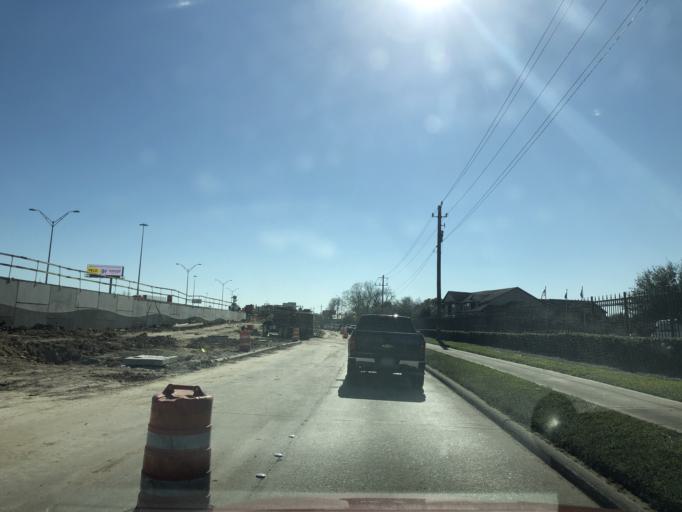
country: US
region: Texas
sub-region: Harris County
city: Deer Park
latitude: 29.6802
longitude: -95.1562
